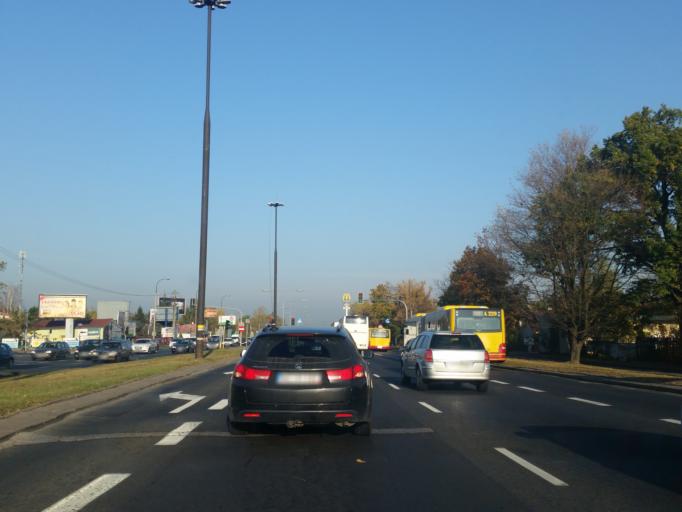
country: PL
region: Masovian Voivodeship
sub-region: Warszawa
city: Bielany
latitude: 52.3054
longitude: 20.9342
